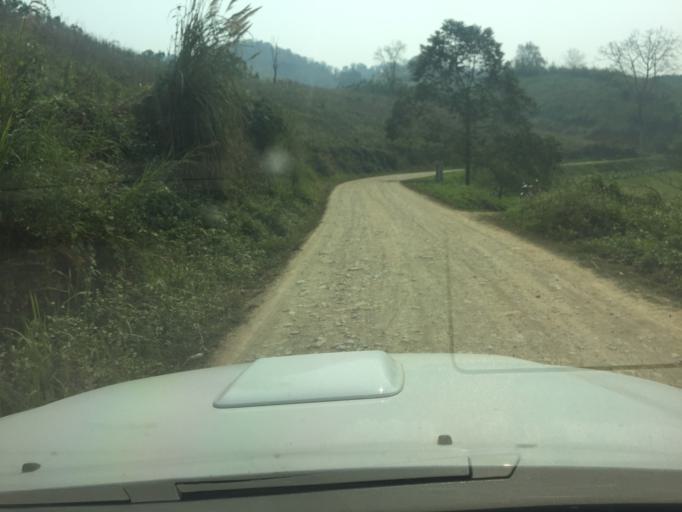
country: TH
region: Phayao
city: Phu Sang
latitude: 19.6159
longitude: 100.5366
